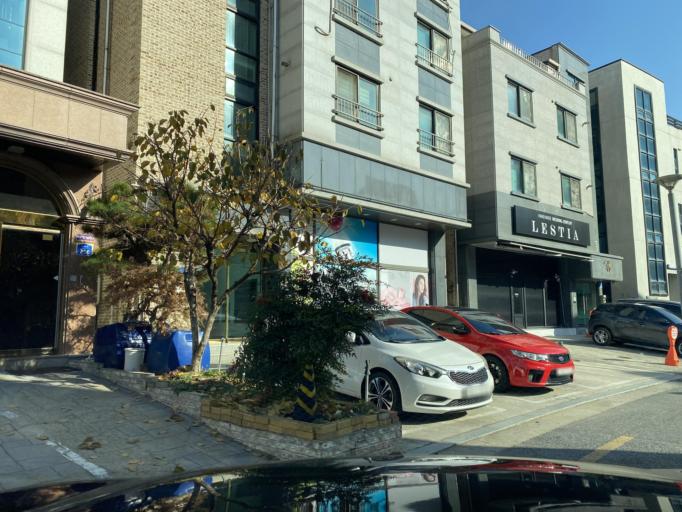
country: KR
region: Chungcheongnam-do
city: Cheonan
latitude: 36.7999
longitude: 127.1069
